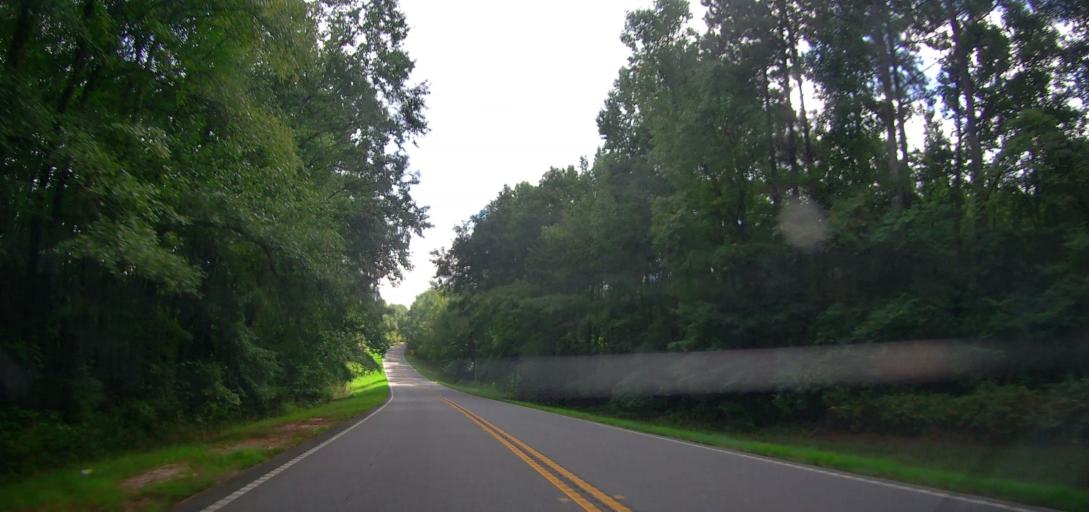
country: US
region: Georgia
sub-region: Talbot County
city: Talbotton
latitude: 32.6290
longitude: -84.4884
